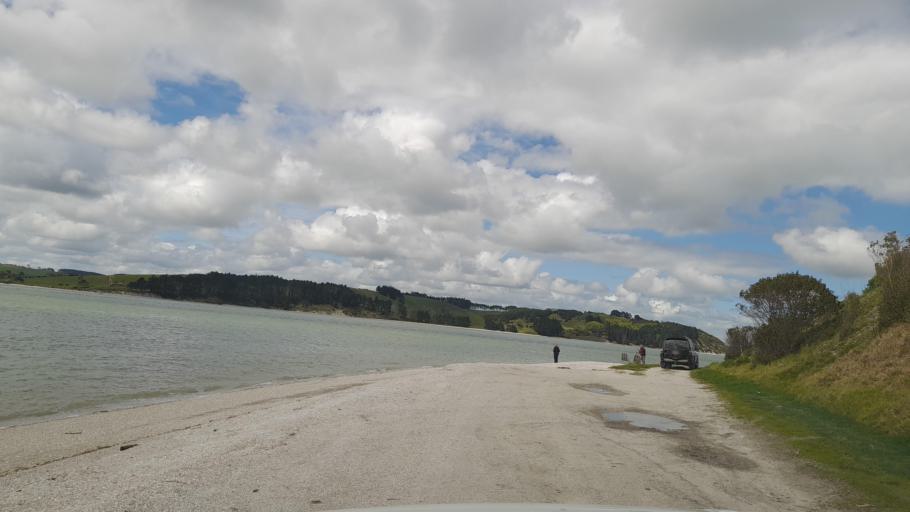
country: NZ
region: Auckland
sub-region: Auckland
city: Wellsford
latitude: -36.2231
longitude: 174.3213
